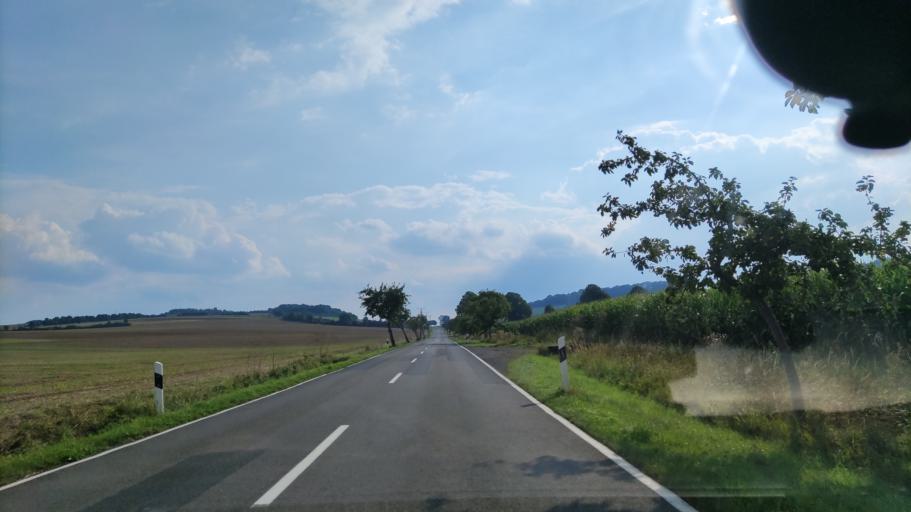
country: DE
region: Lower Saxony
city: Dassel
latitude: 51.8198
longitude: 9.7133
